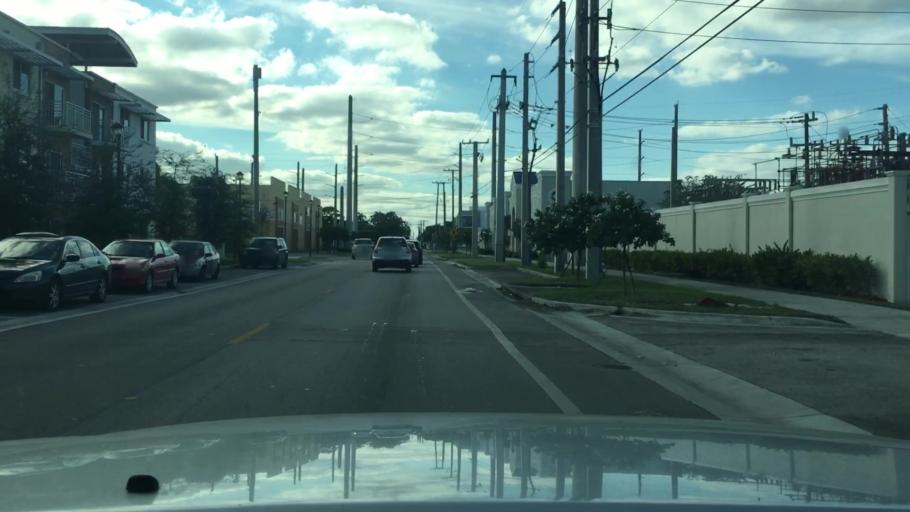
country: US
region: Florida
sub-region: Miami-Dade County
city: Princeton
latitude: 25.5366
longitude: -80.4028
